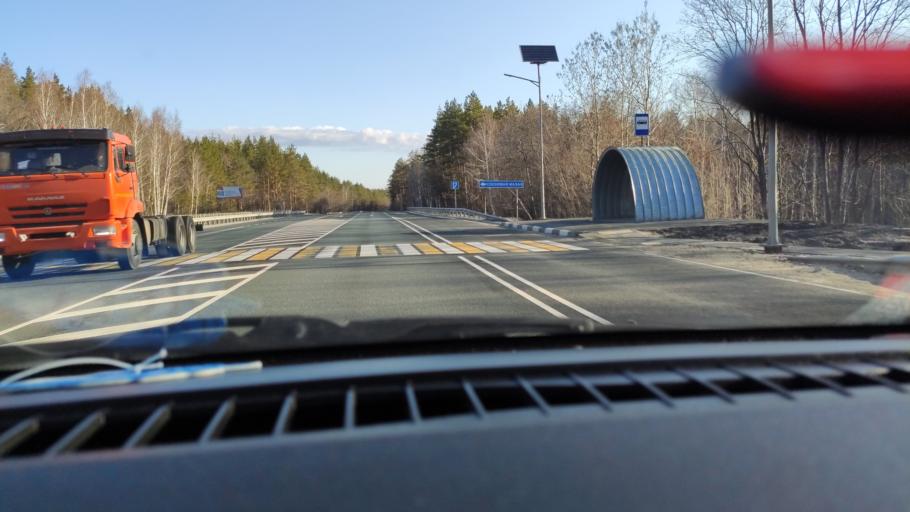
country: RU
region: Saratov
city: Khvalynsk
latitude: 52.5146
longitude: 48.0168
